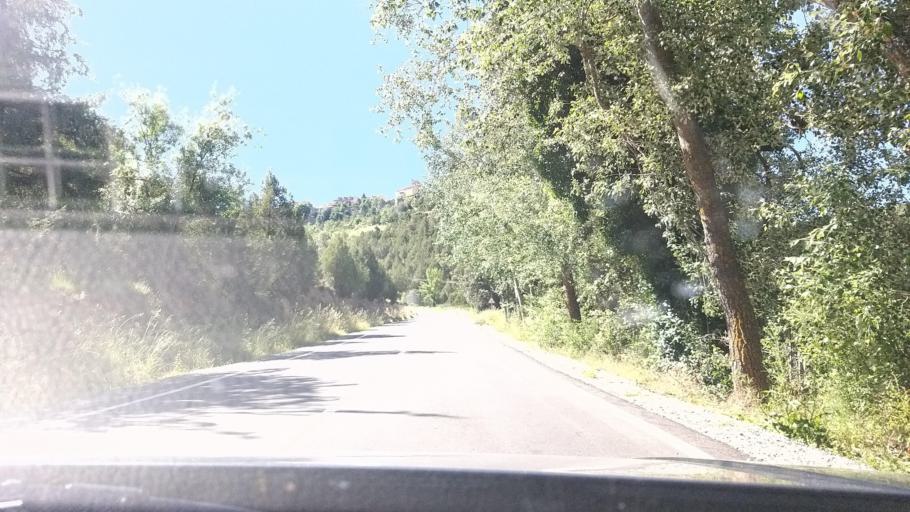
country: ES
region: Castille and Leon
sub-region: Provincia de Segovia
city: Pedraza
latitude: 41.1359
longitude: -3.8151
